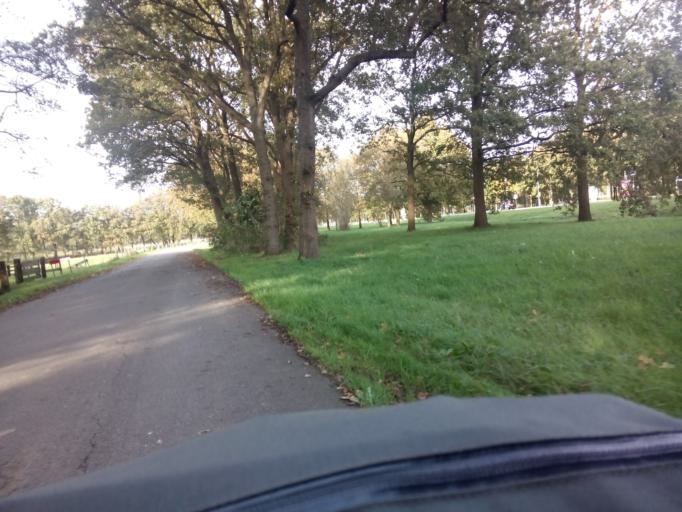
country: NL
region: Drenthe
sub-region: Gemeente Assen
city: Assen
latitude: 52.9744
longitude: 6.5552
